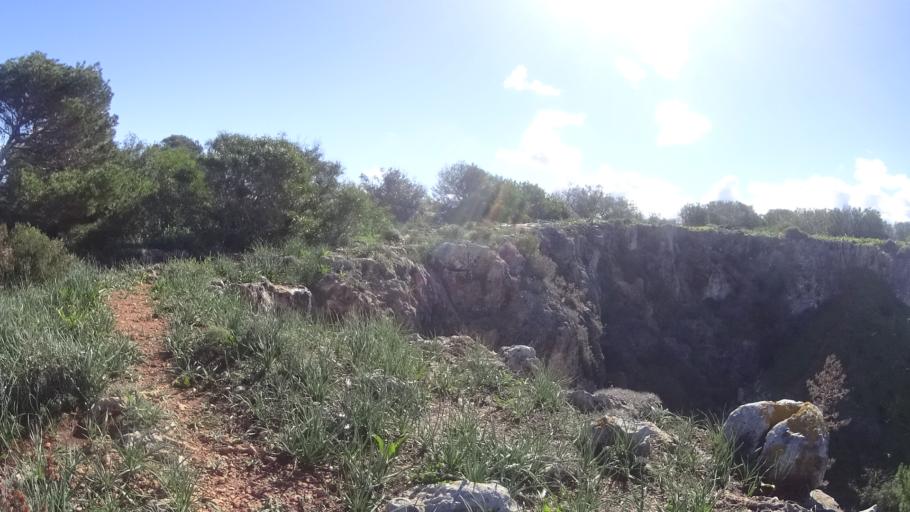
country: MT
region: Saint Paul's Bay
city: San Pawl il-Bahar
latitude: 35.9567
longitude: 14.3904
